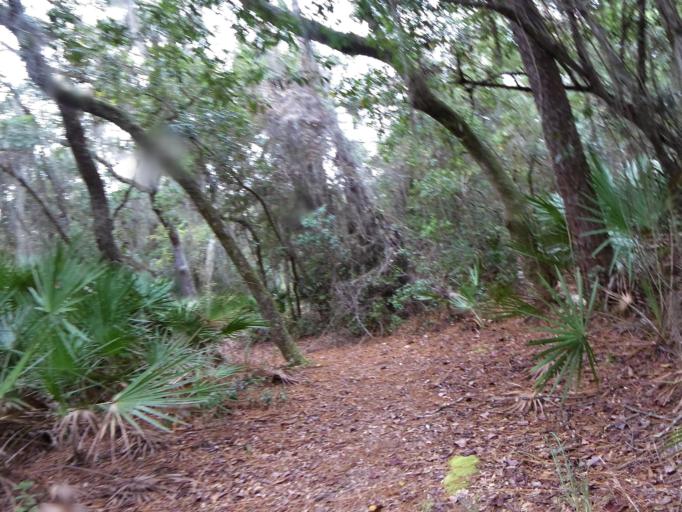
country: US
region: Georgia
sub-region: Charlton County
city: Folkston
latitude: 30.7152
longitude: -82.1544
